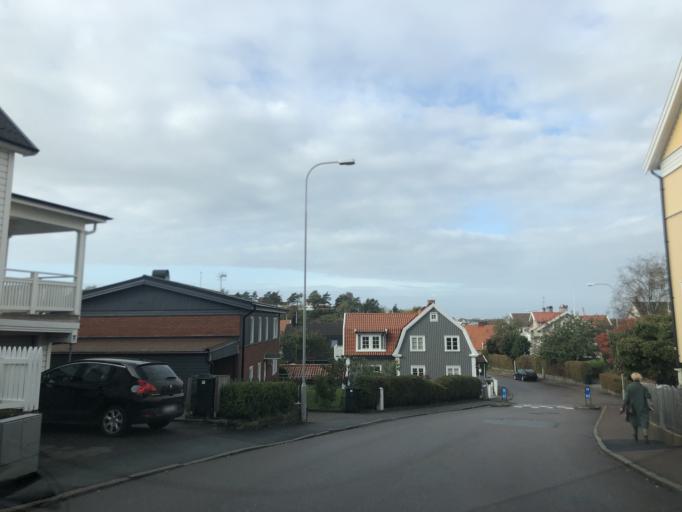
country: SE
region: Vaestra Goetaland
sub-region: Goteborg
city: Majorna
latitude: 57.6755
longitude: 11.9043
